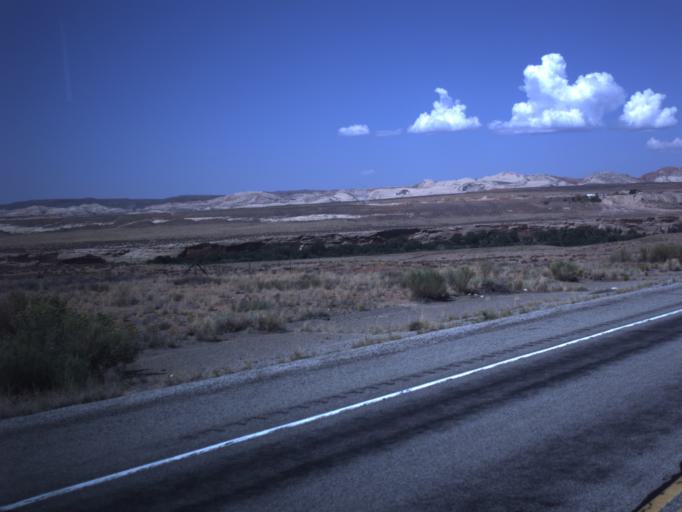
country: US
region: Utah
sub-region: San Juan County
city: Blanding
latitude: 37.2510
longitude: -109.6120
